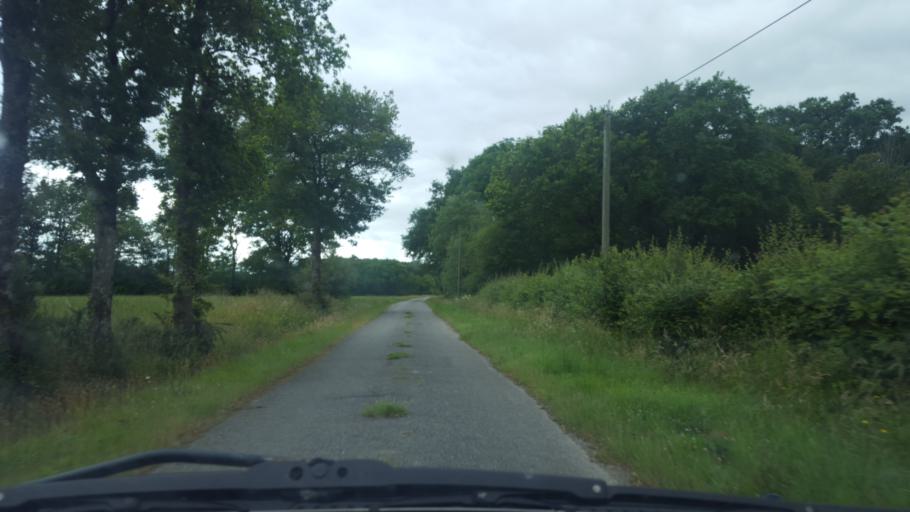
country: FR
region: Pays de la Loire
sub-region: Departement de la Loire-Atlantique
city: Saint-Philbert-de-Grand-Lieu
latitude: 47.0130
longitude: -1.6815
